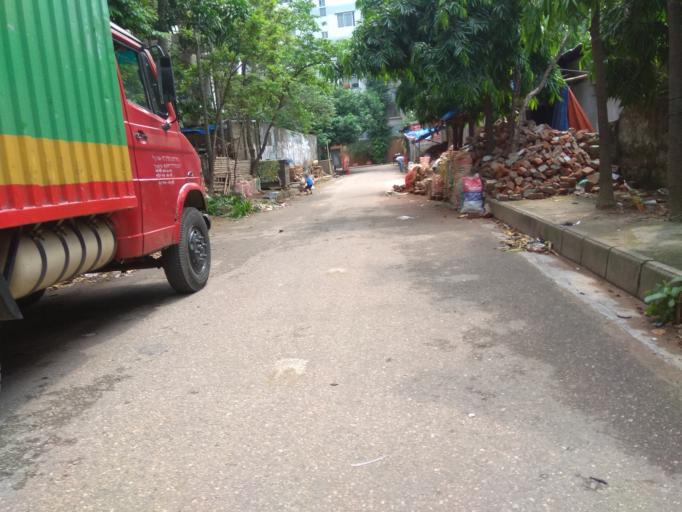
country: BD
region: Dhaka
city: Azimpur
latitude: 23.8019
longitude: 90.3563
